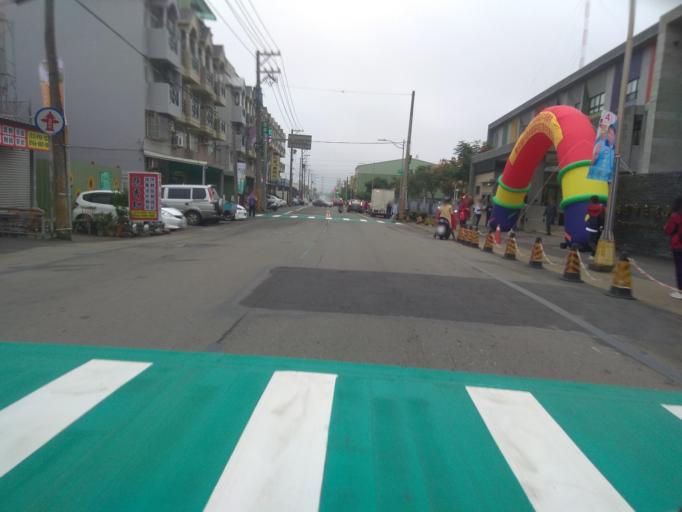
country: TW
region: Taiwan
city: Taoyuan City
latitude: 25.0146
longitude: 121.1330
